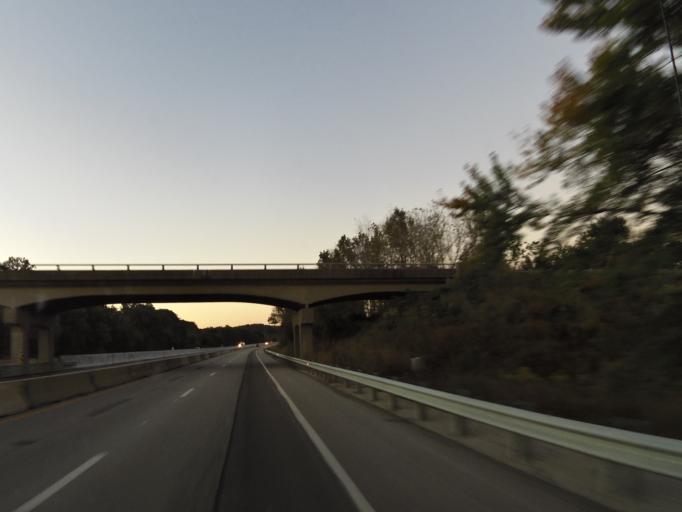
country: US
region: Kentucky
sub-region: Rockcastle County
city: Brodhead
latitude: 37.4663
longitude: -84.3351
